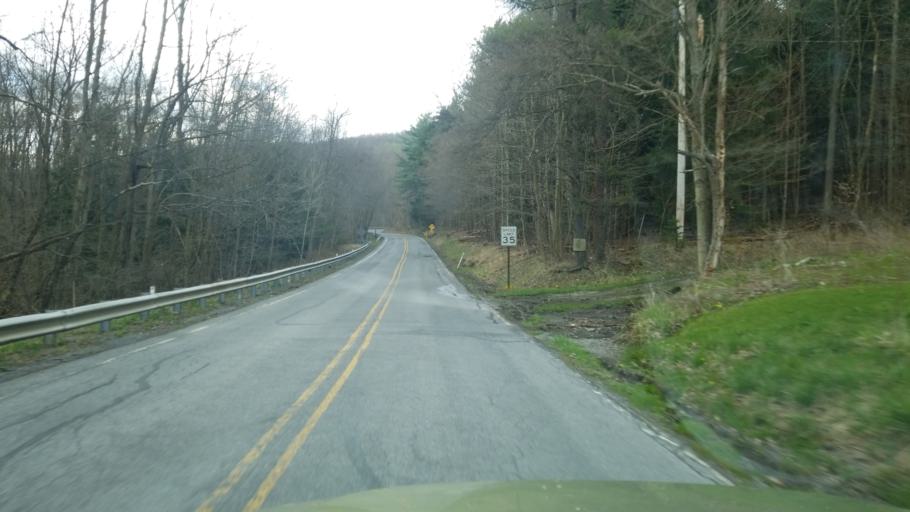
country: US
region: Pennsylvania
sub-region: Clearfield County
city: Curwensville
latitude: 40.8876
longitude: -78.4602
